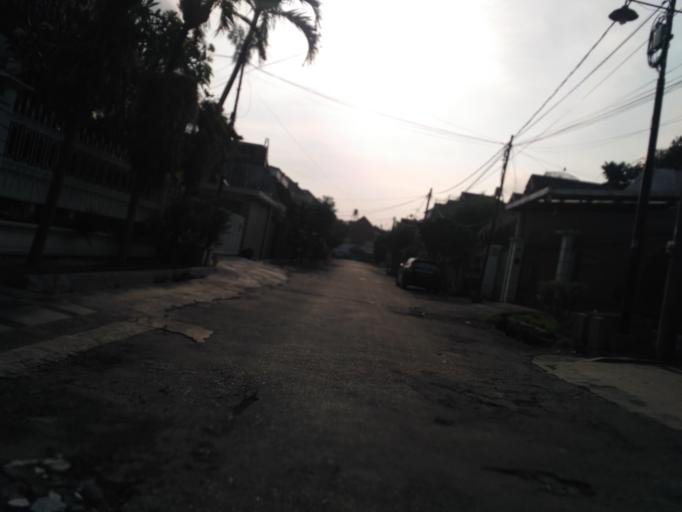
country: ID
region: East Java
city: Malang
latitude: -7.9362
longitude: 112.6353
